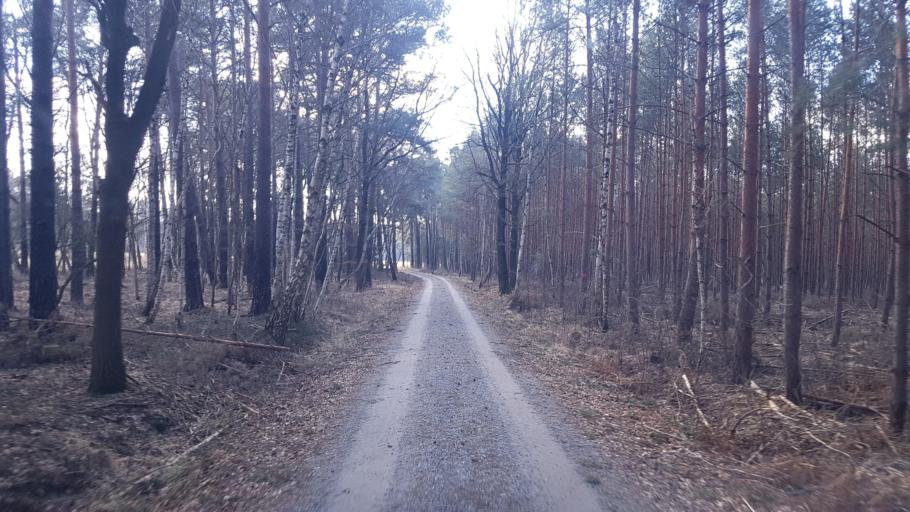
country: DE
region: Brandenburg
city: Plessa
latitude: 51.5197
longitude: 13.6240
